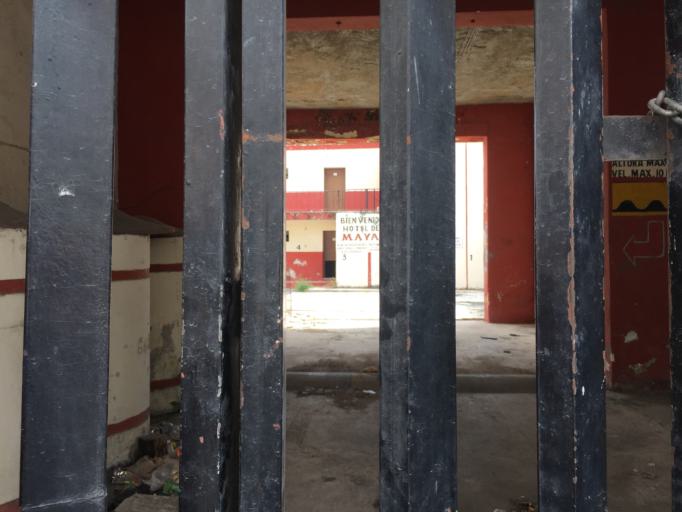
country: MX
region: Yucatan
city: Merida
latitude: 20.9637
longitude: -89.6173
